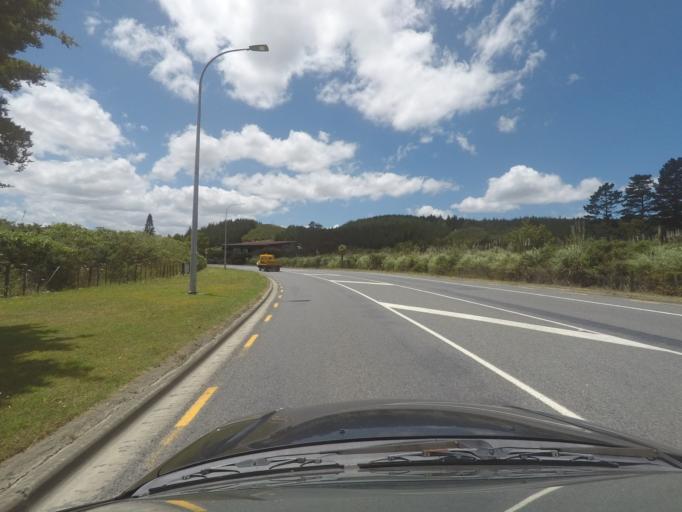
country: NZ
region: Northland
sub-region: Whangarei
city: Whangarei
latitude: -35.7518
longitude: 174.3199
